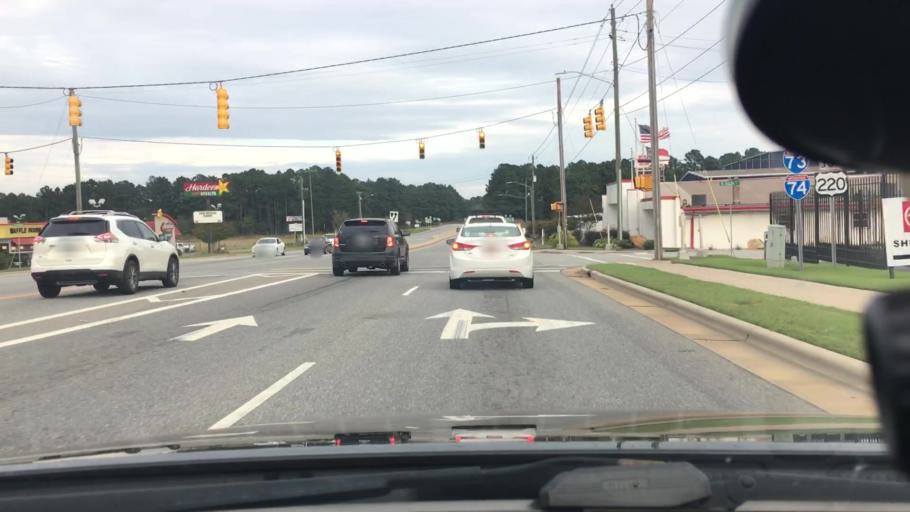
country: US
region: North Carolina
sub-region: Montgomery County
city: Biscoe
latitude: 35.3605
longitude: -79.7700
